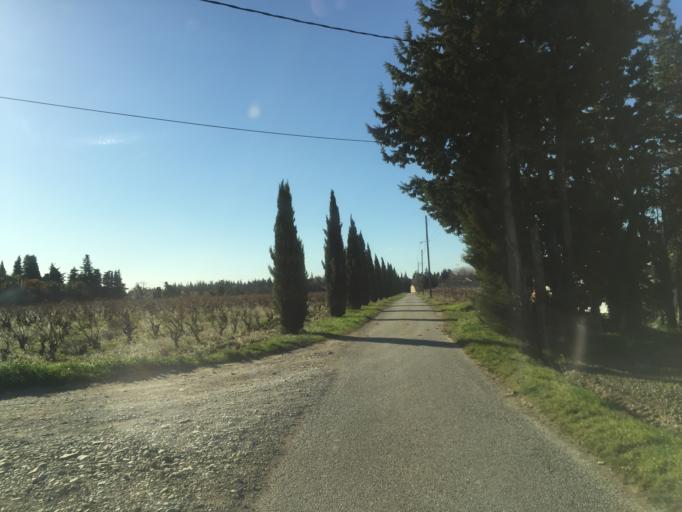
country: FR
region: Provence-Alpes-Cote d'Azur
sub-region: Departement du Vaucluse
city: Courthezon
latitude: 44.0842
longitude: 4.9103
